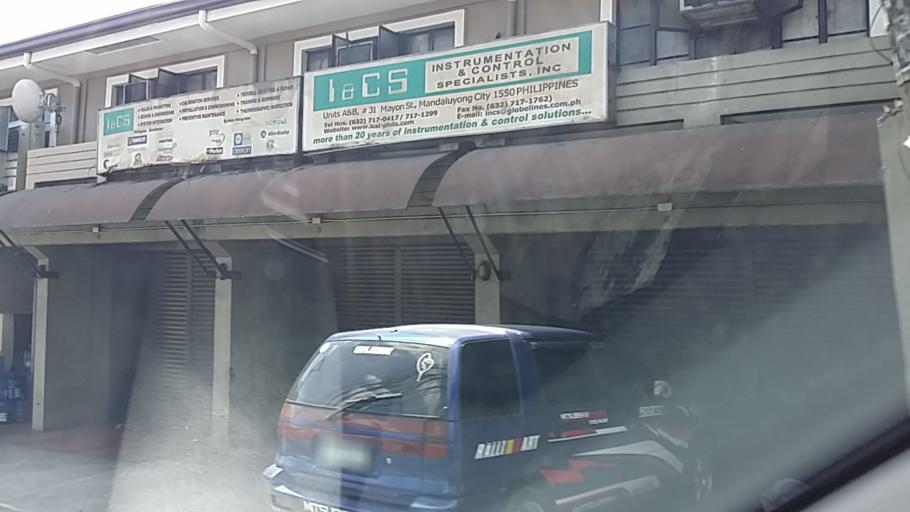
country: PH
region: Metro Manila
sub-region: Mandaluyong
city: Mandaluyong City
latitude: 14.5742
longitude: 121.0459
